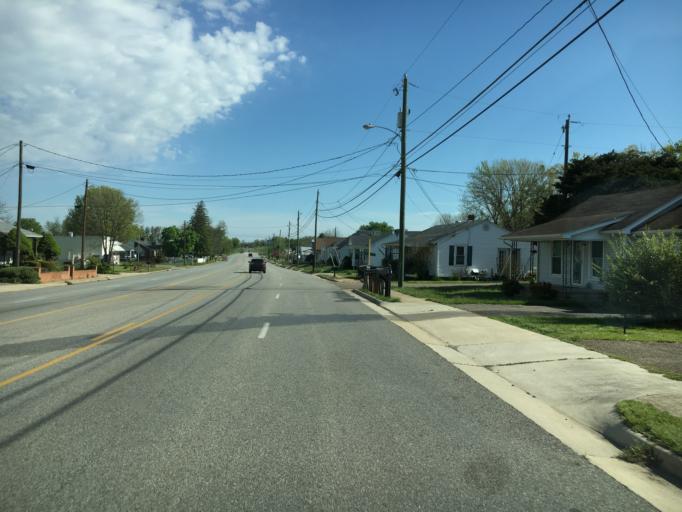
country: US
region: Virginia
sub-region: Augusta County
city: Dooms
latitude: 38.1084
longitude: -78.8576
